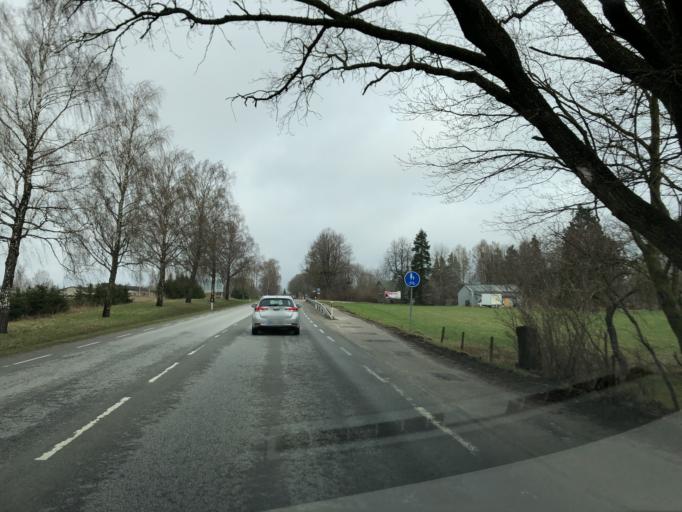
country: EE
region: Jogevamaa
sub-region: Jogeva linn
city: Jogeva
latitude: 58.7353
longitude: 26.3752
